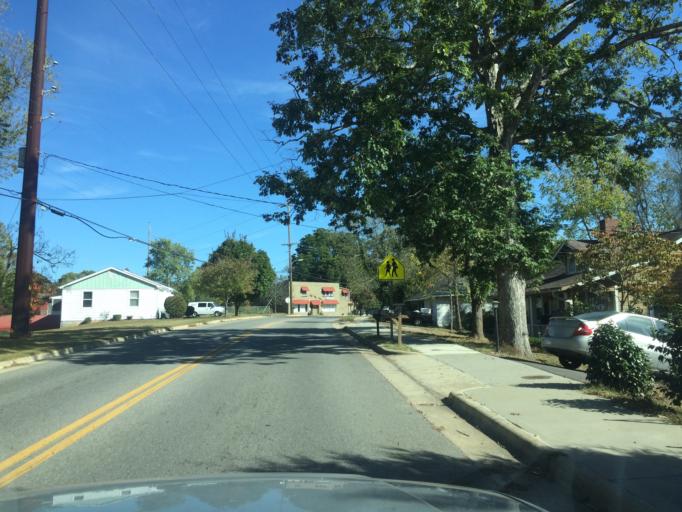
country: US
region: North Carolina
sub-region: Buncombe County
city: Woodfin
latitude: 35.6340
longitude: -82.5864
